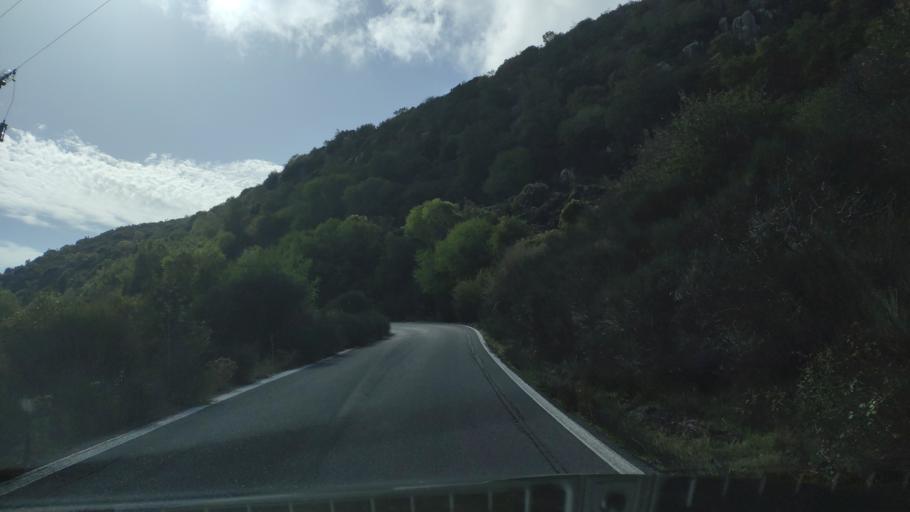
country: GR
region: Peloponnese
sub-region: Nomos Arkadias
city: Dimitsana
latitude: 37.5839
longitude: 22.0187
